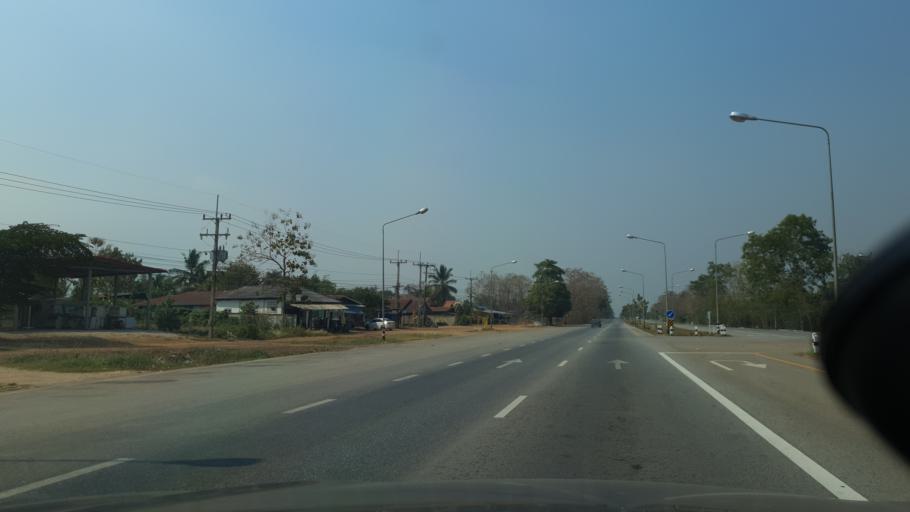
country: TH
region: Kamphaeng Phet
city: Kosamphi Nakhon
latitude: 16.5923
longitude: 99.4214
